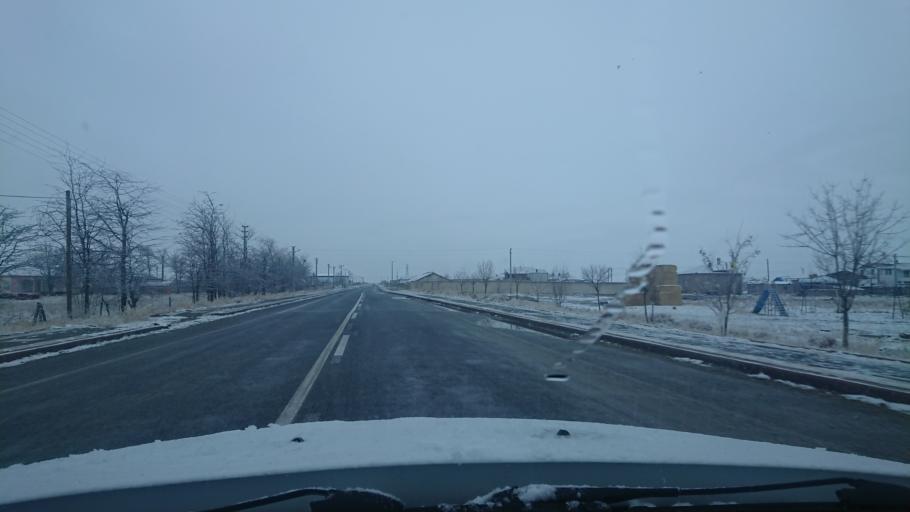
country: TR
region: Aksaray
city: Yesilova
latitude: 38.2928
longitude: 33.7598
